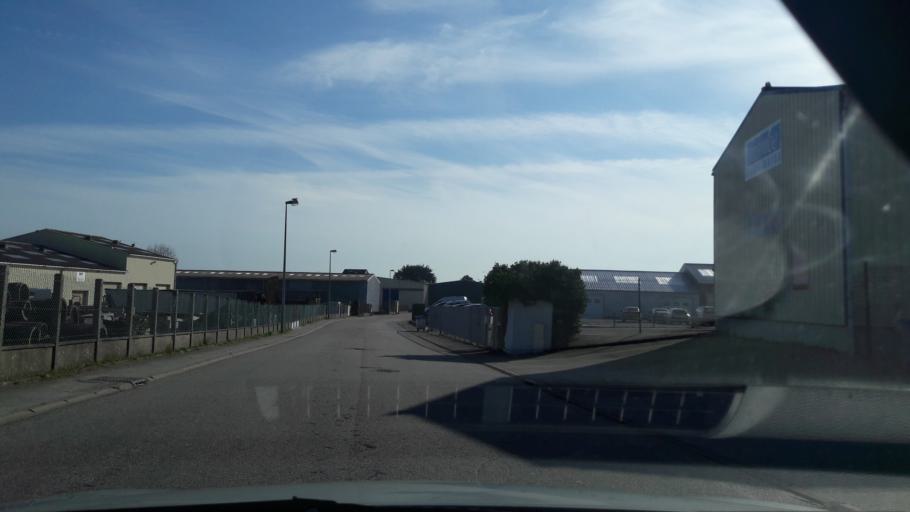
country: FR
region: Lower Normandy
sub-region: Departement de la Manche
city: Querqueville
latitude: 49.6593
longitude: -1.6855
